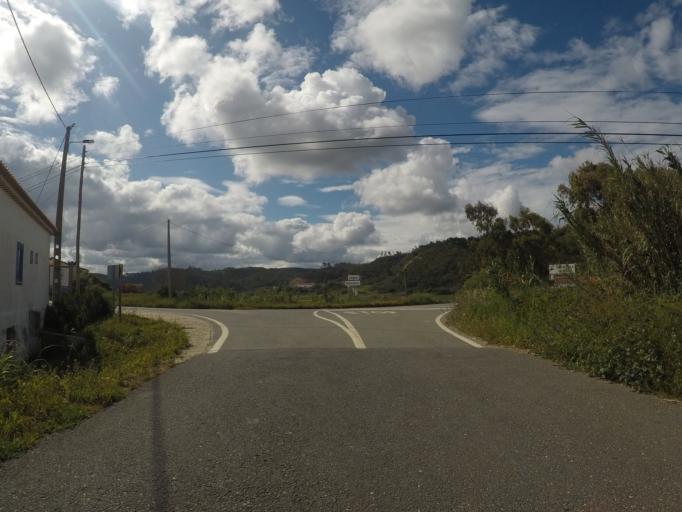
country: PT
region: Beja
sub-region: Odemira
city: Sao Teotonio
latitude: 37.4355
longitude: -8.7647
